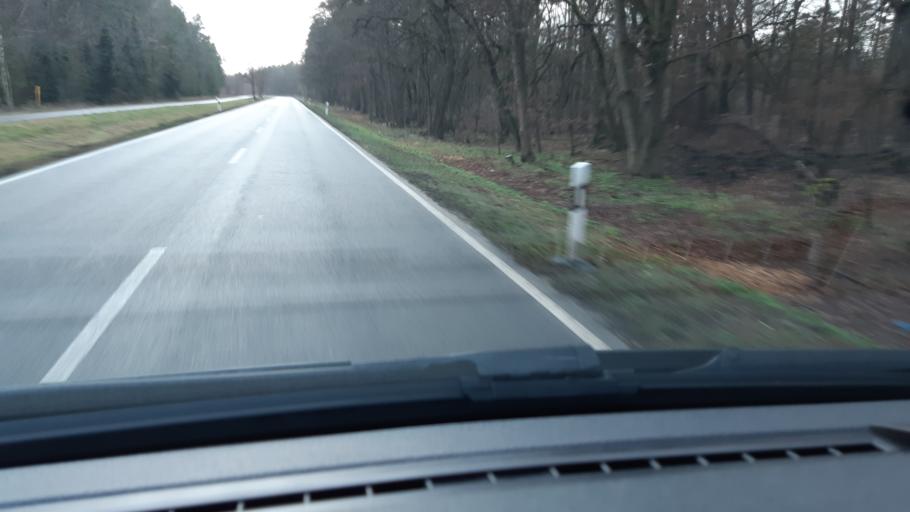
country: DE
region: Brandenburg
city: Zehdenick
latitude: 53.0542
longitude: 13.4038
